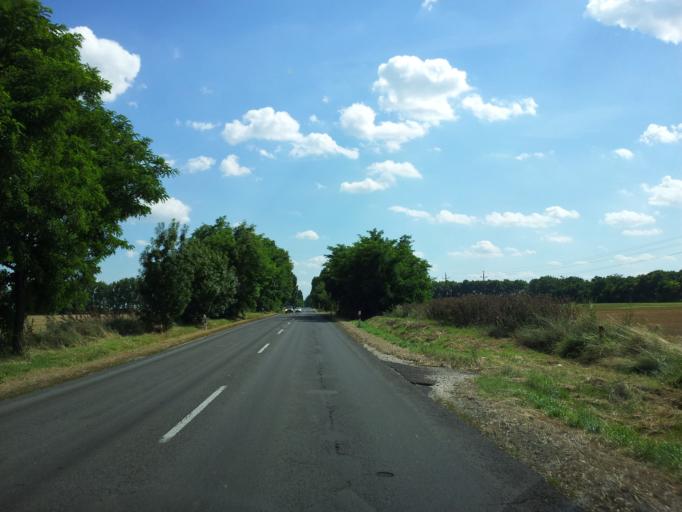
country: HU
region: Pest
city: Dunavarsany
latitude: 47.2526
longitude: 19.0245
